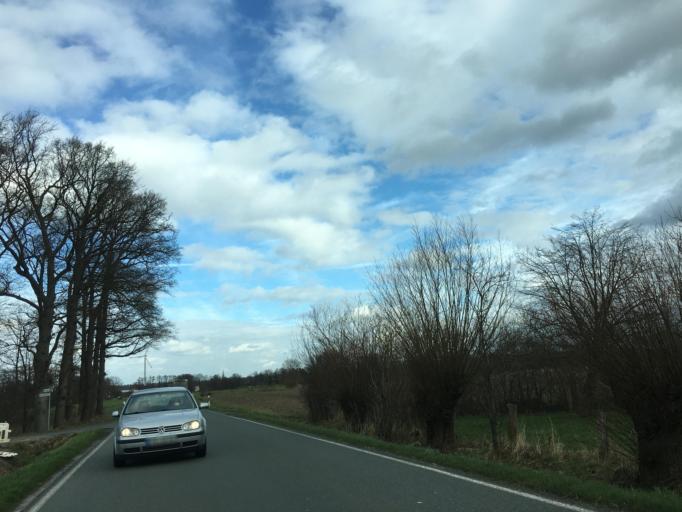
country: DE
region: North Rhine-Westphalia
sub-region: Regierungsbezirk Munster
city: Altenberge
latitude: 52.0201
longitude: 7.4443
